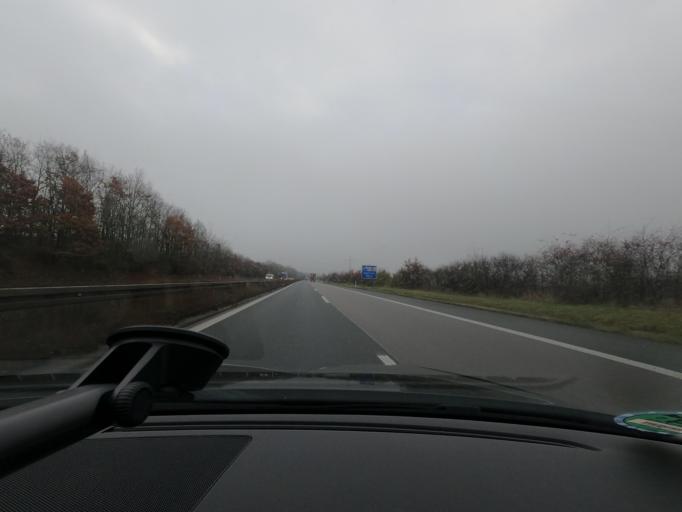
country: DE
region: Bavaria
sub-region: Upper Franconia
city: Eggolsheim
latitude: 49.7631
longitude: 11.0531
